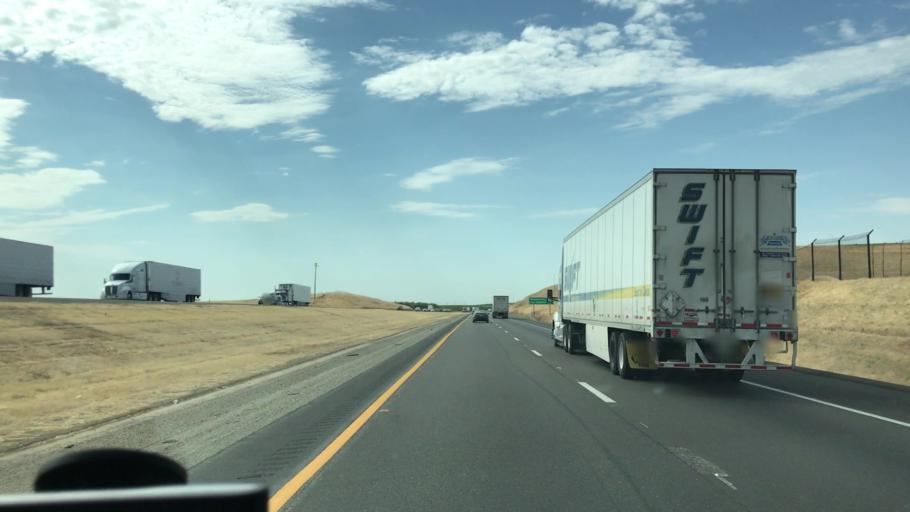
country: US
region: California
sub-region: Stanislaus County
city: Patterson
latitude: 37.3902
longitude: -121.1332
